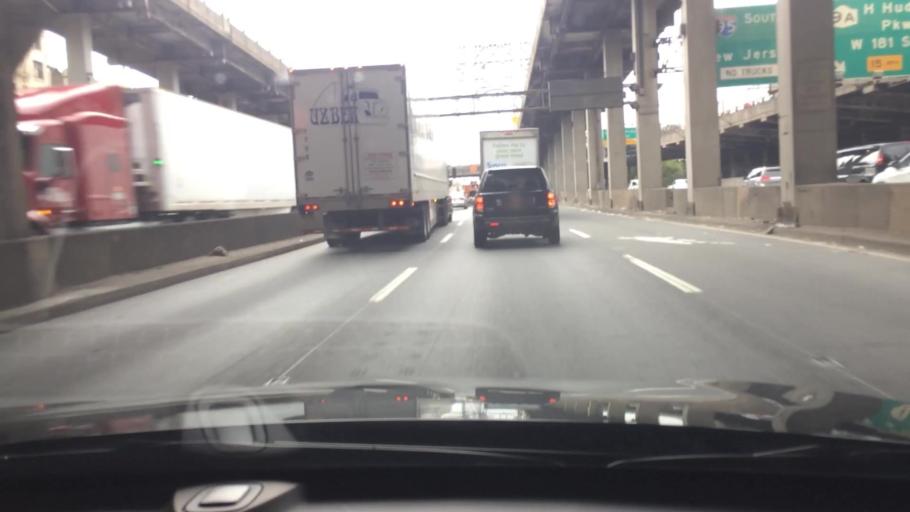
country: US
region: New York
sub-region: New York County
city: Inwood
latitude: 40.8511
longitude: -73.9412
